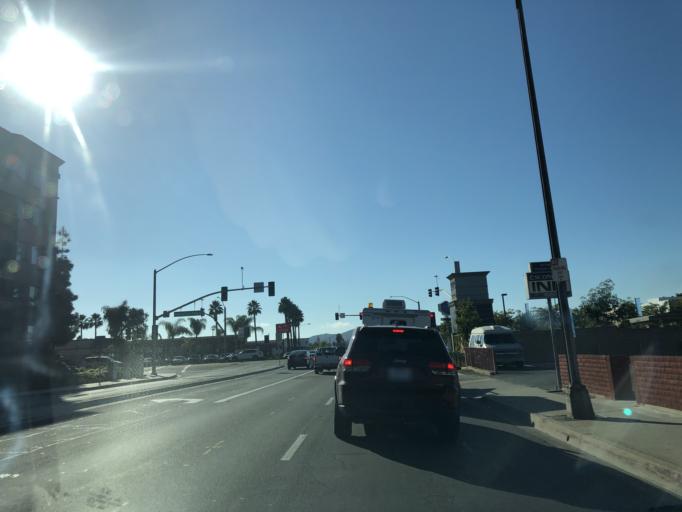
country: US
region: California
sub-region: San Diego County
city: Escondido
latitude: 33.1254
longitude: -117.0892
